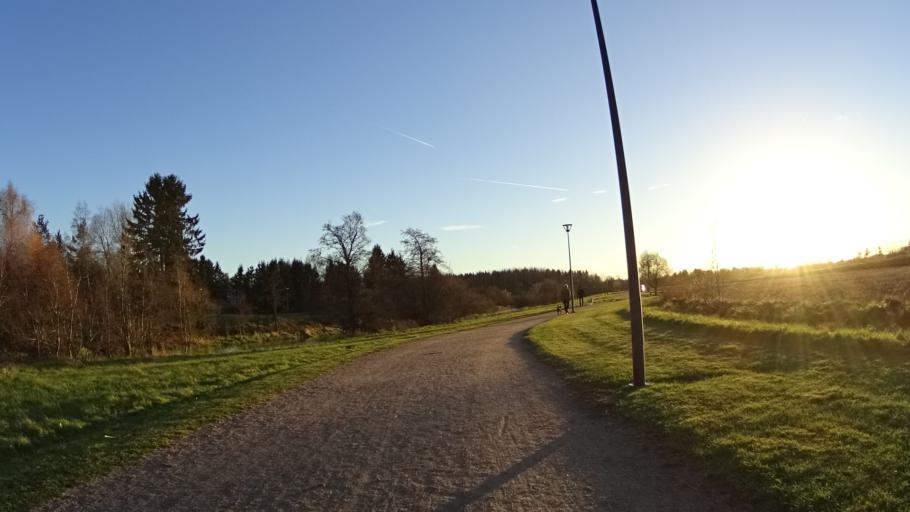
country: FI
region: Uusimaa
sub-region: Helsinki
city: Vantaa
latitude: 60.2846
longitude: 24.9988
